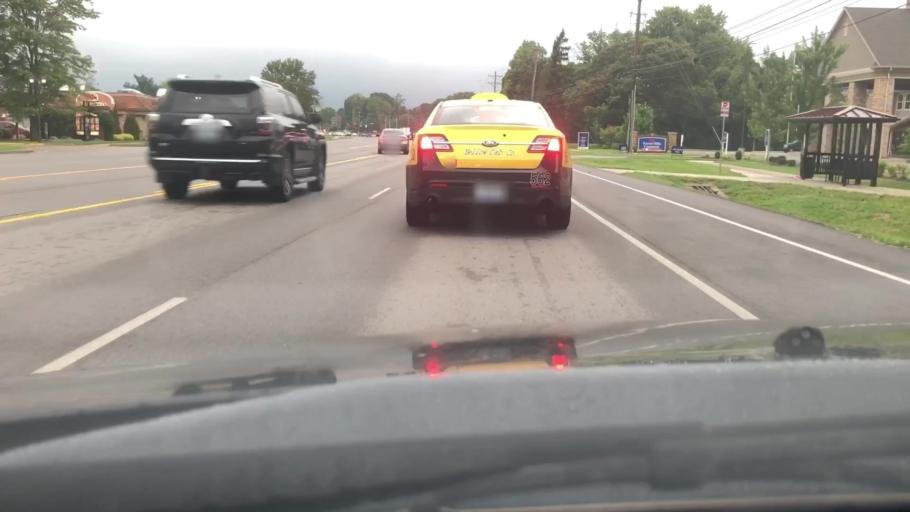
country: US
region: Kentucky
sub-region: Jefferson County
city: Hurstbourne Acres
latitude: 38.2129
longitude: -85.5878
